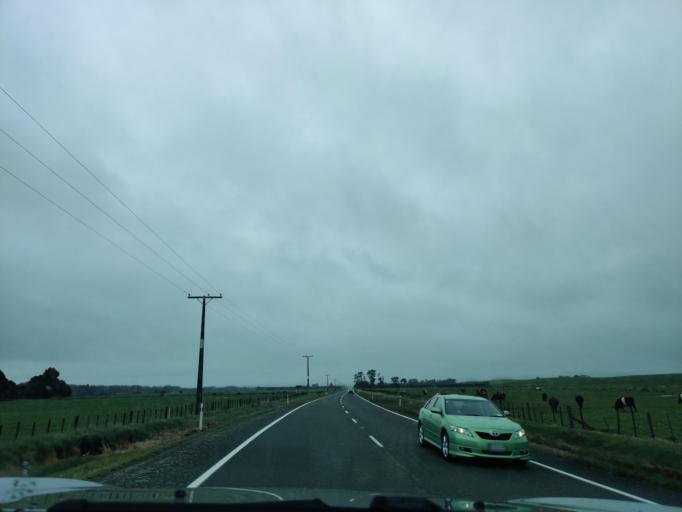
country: NZ
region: Hawke's Bay
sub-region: Hastings District
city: Hastings
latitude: -40.0199
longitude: 176.2757
